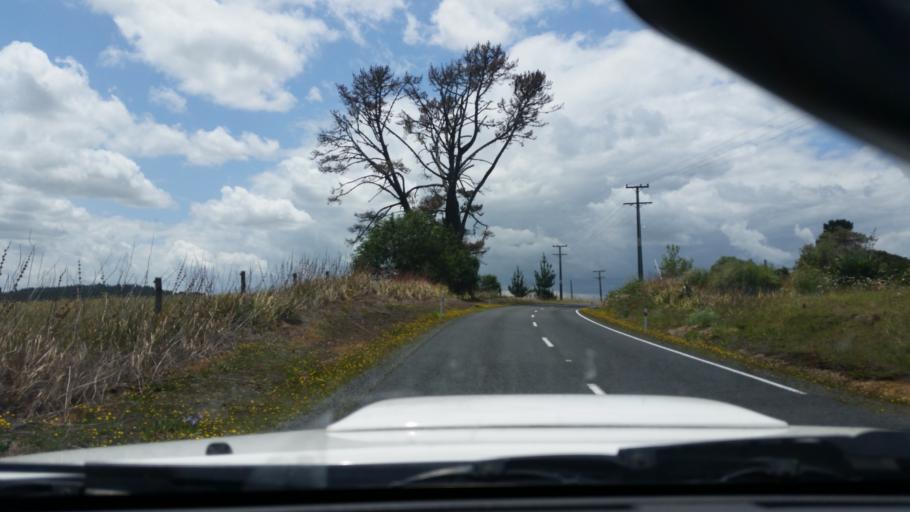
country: NZ
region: Northland
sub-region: Kaipara District
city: Dargaville
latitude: -35.9161
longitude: 173.8238
